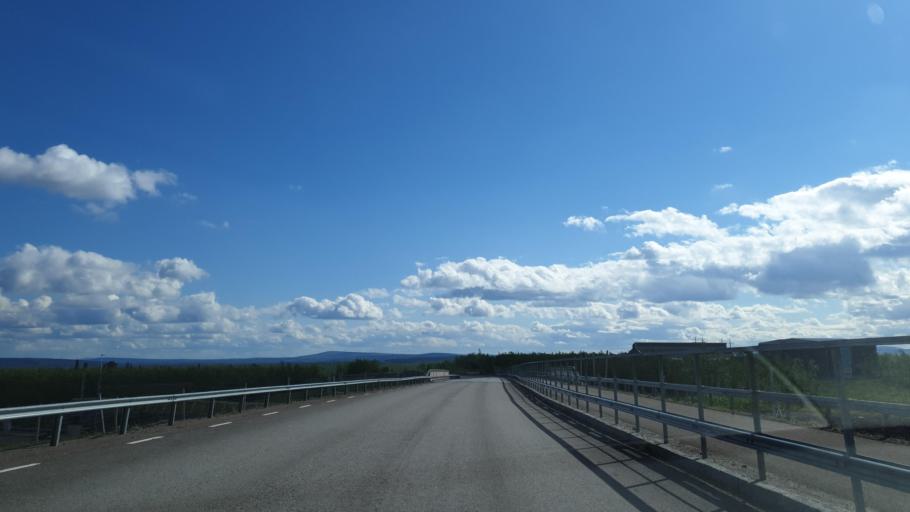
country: SE
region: Norrbotten
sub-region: Kiruna Kommun
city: Kiruna
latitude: 67.7957
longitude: 20.2335
